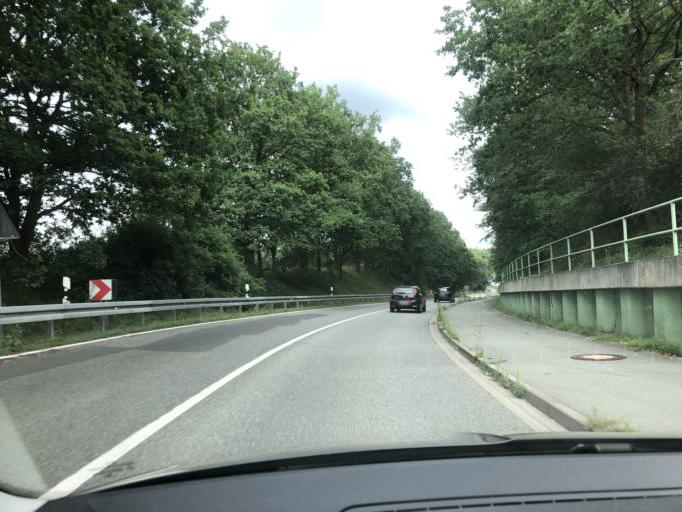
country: DE
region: Mecklenburg-Vorpommern
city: Neumuehle
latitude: 53.6230
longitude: 11.3570
